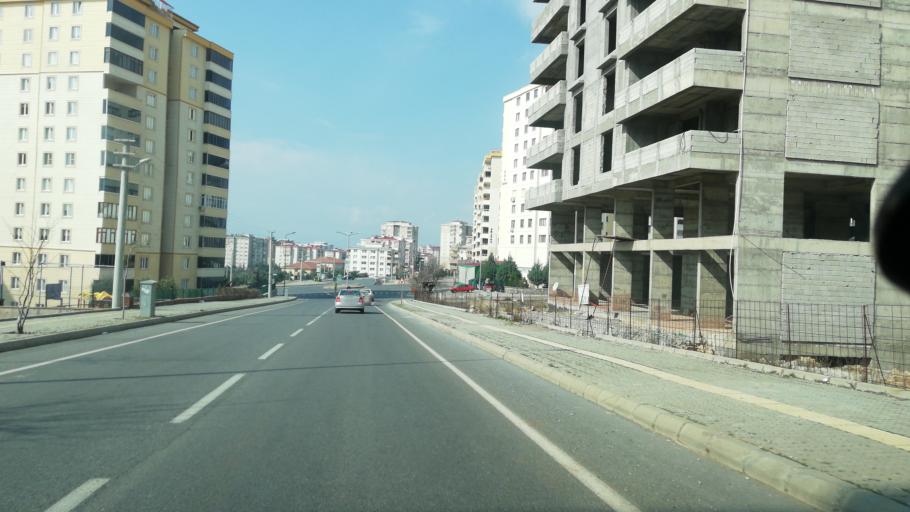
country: TR
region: Kahramanmaras
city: Kahramanmaras
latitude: 37.5867
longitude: 36.8711
